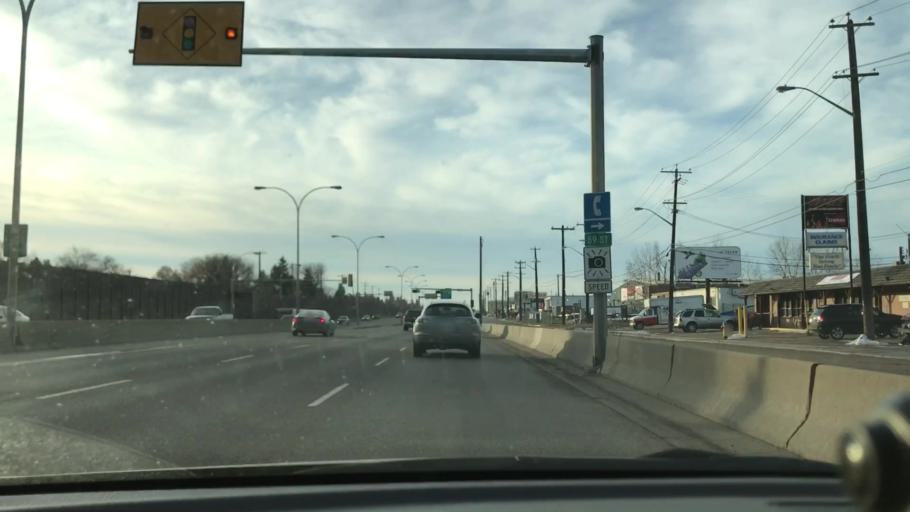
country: CA
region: Alberta
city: Edmonton
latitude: 53.5814
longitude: -113.4762
